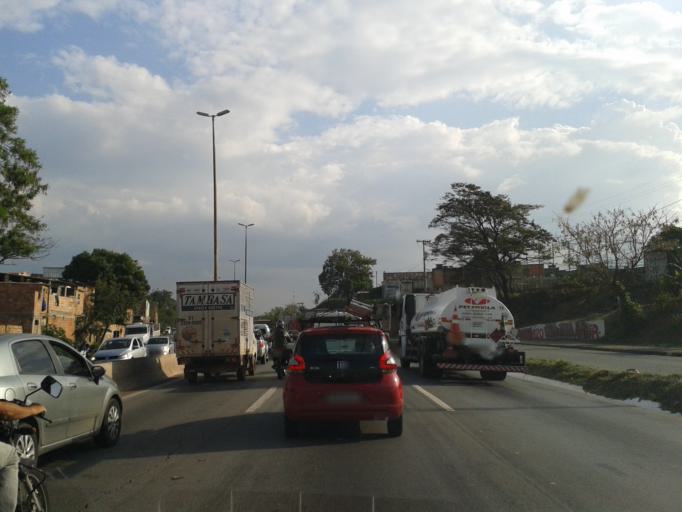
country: BR
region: Minas Gerais
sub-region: Belo Horizonte
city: Belo Horizonte
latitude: -19.8728
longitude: -43.9490
